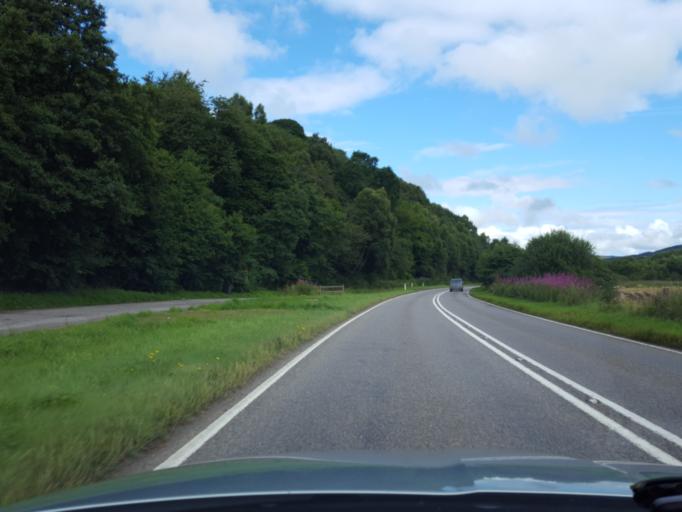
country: GB
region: Scotland
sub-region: Moray
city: Rothes
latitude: 57.5096
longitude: -3.2031
